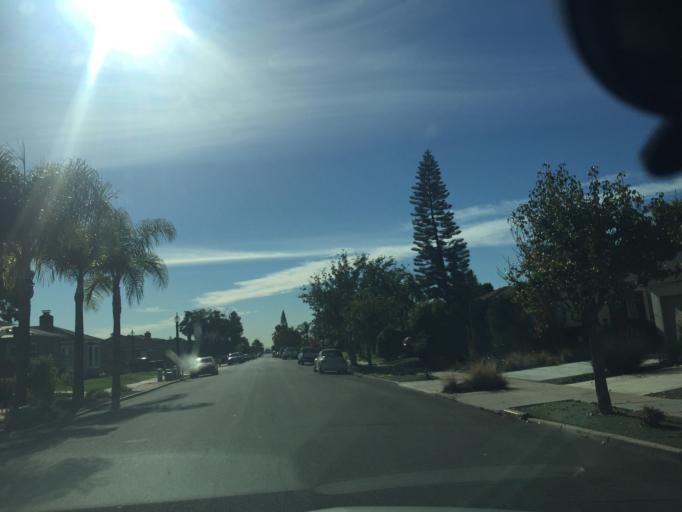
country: US
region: California
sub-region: San Diego County
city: Lemon Grove
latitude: 32.7617
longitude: -117.0889
